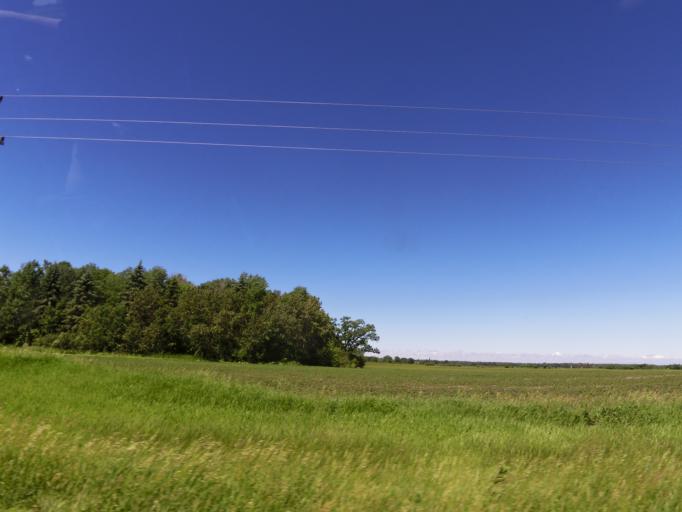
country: US
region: Minnesota
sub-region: Polk County
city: Fosston
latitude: 47.5835
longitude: -95.9823
